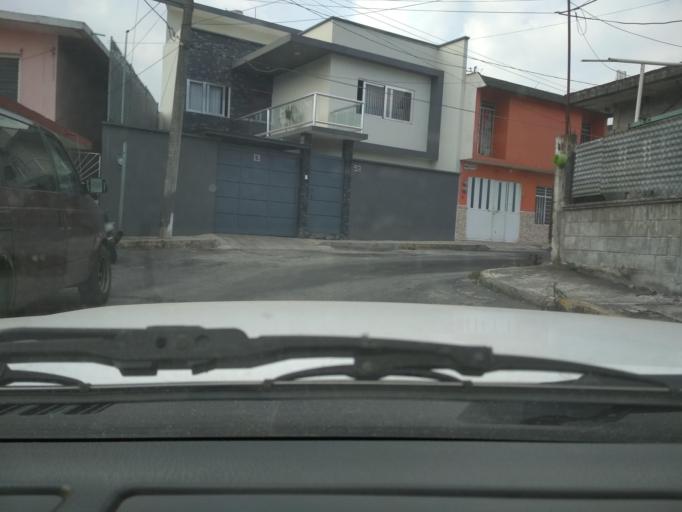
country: MX
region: Veracruz
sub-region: Mariano Escobedo
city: Palmira
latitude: 18.8707
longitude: -97.1016
